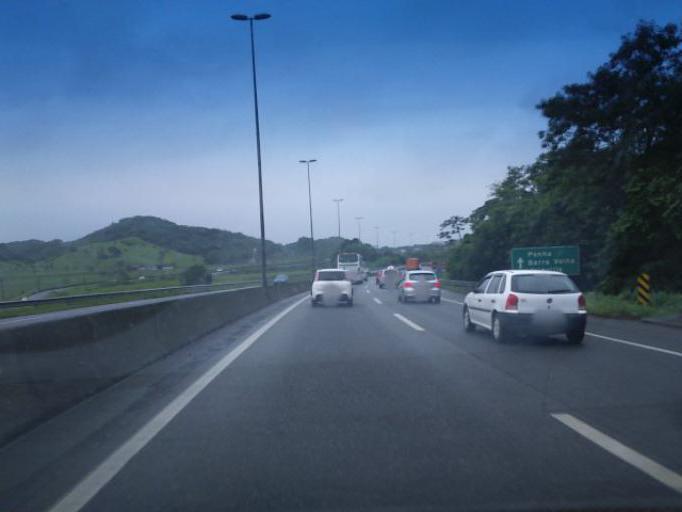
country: BR
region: Santa Catarina
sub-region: Penha
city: Penha
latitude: -26.8107
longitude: -48.6830
